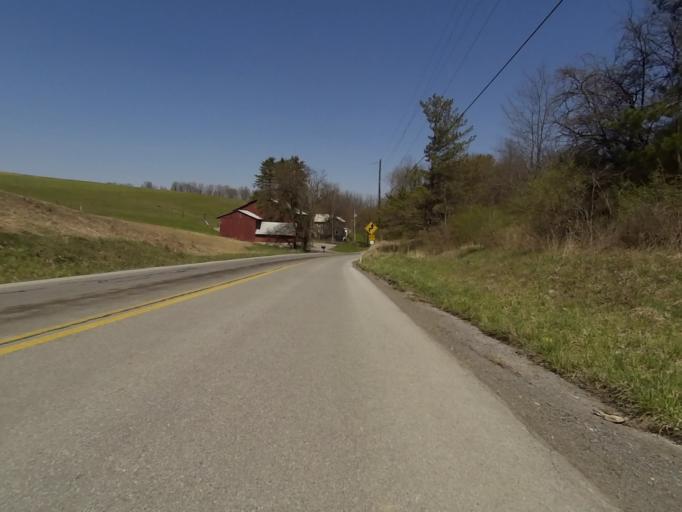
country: US
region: Pennsylvania
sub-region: Blair County
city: Tyrone
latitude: 40.5986
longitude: -78.1343
